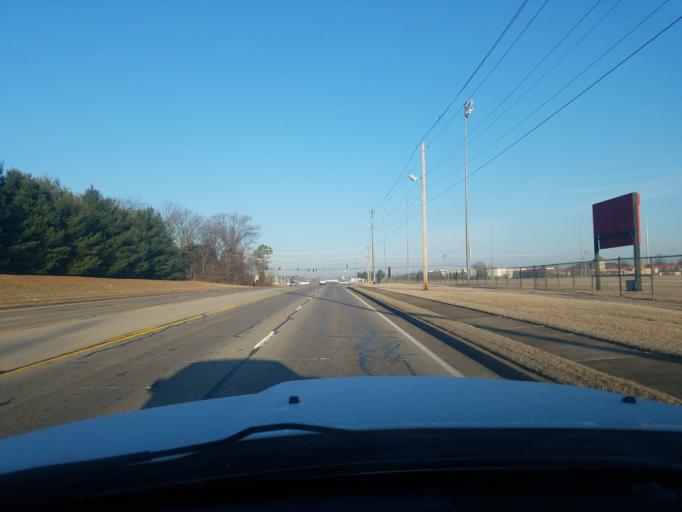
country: US
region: Kentucky
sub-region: Warren County
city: Bowling Green
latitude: 36.9643
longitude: -86.4724
